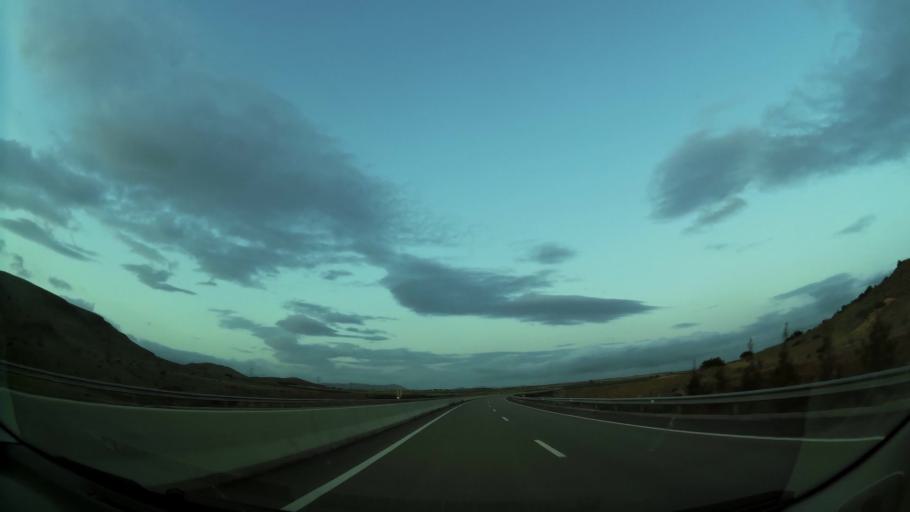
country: MA
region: Oriental
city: El Aioun
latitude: 34.6086
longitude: -2.5783
